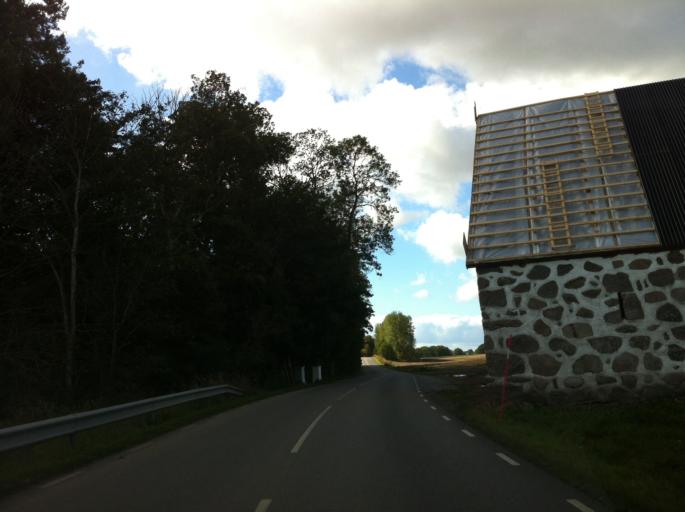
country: SE
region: Skane
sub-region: Tomelilla Kommun
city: Tomelilla
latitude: 55.6500
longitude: 13.9608
